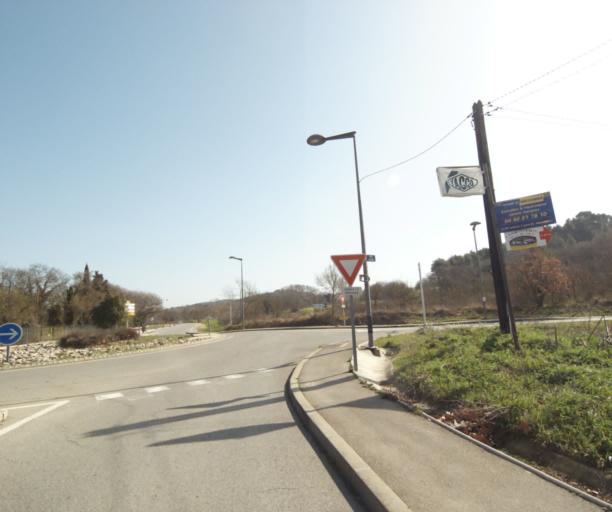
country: FR
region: Provence-Alpes-Cote d'Azur
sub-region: Departement des Bouches-du-Rhone
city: Aix-en-Provence
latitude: 43.5080
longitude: 5.4254
